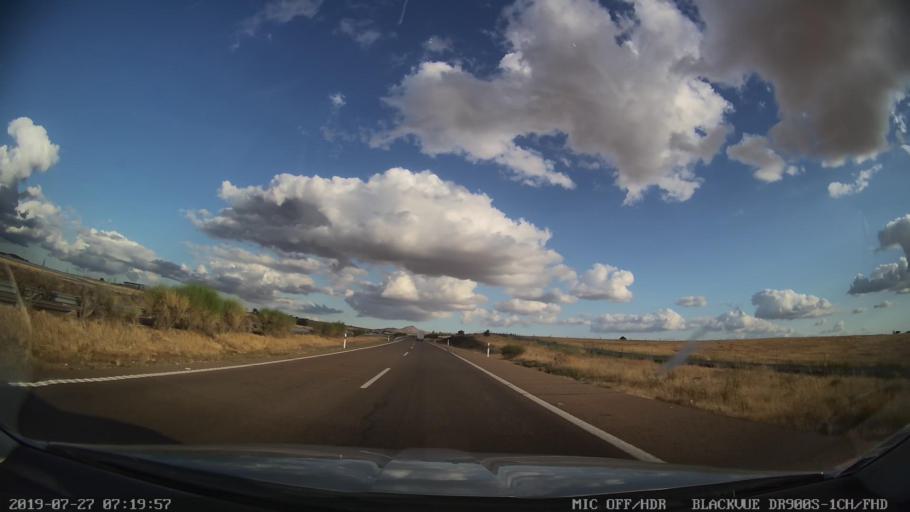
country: ES
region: Extremadura
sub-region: Provincia de Caceres
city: Trujillo
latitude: 39.3905
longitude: -5.8862
